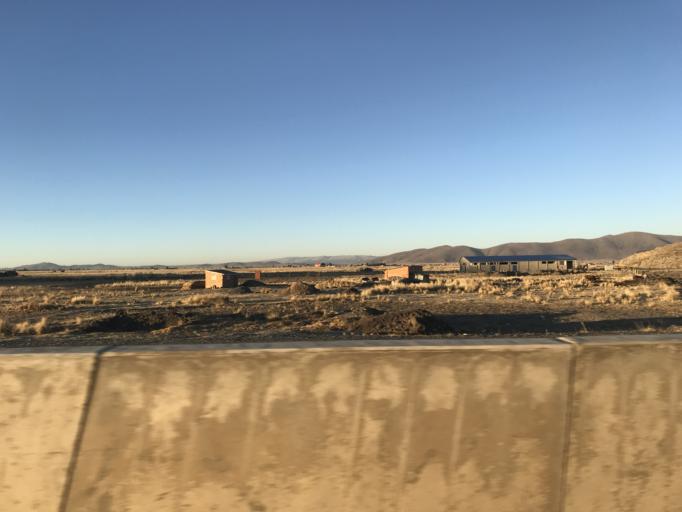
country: BO
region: La Paz
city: Batallas
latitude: -16.2984
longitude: -68.5221
